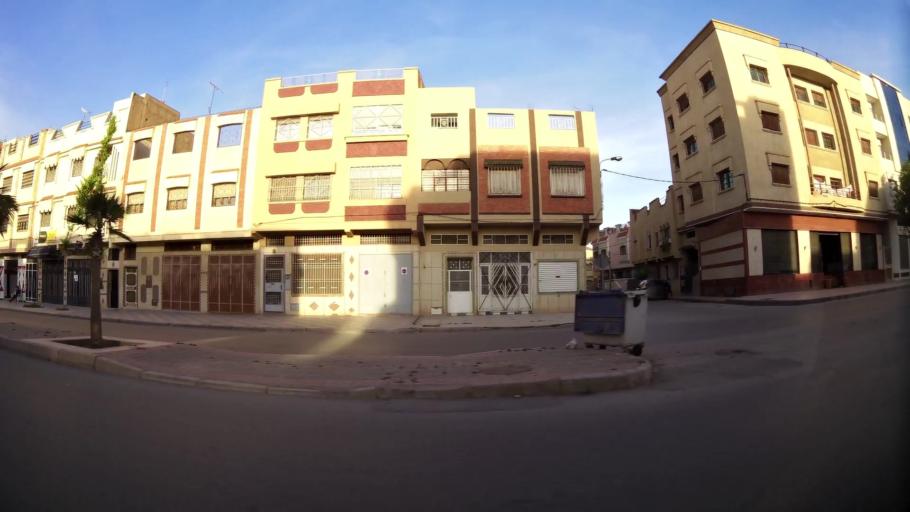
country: MA
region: Oriental
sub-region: Oujda-Angad
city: Oujda
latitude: 34.6754
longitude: -1.8921
